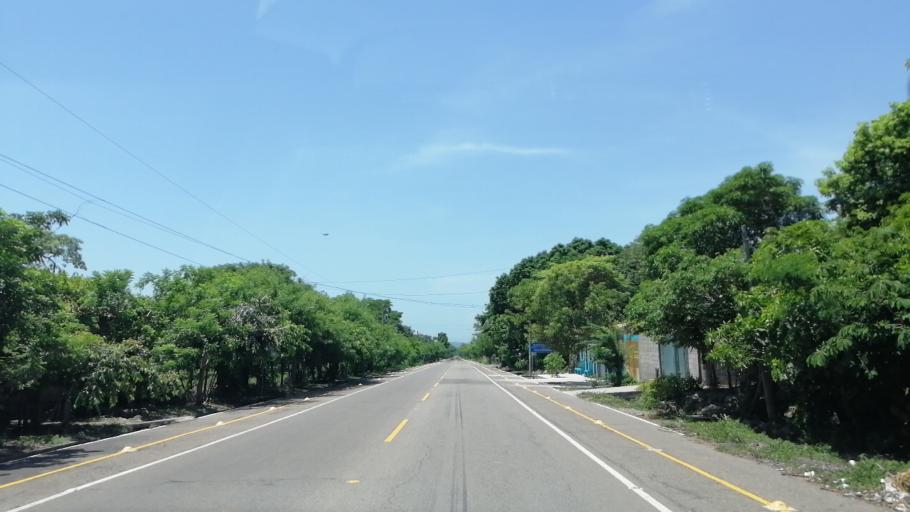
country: SV
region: Chalatenango
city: Nueva Concepcion
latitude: 14.1431
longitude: -89.2997
